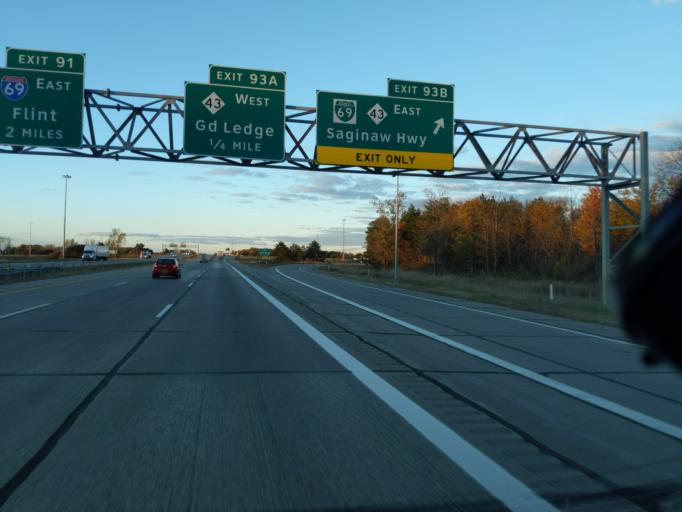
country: US
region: Michigan
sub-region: Eaton County
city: Waverly
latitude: 42.7360
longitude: -84.6682
